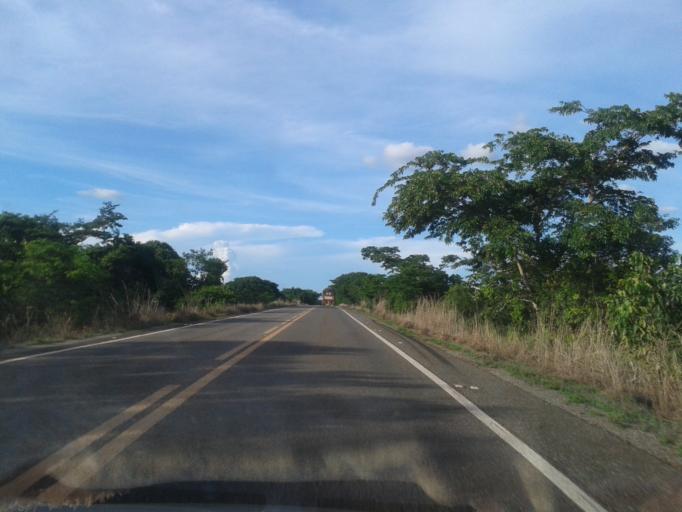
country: BR
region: Goias
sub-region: Sao Miguel Do Araguaia
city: Sao Miguel do Araguaia
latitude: -13.6973
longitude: -50.3319
